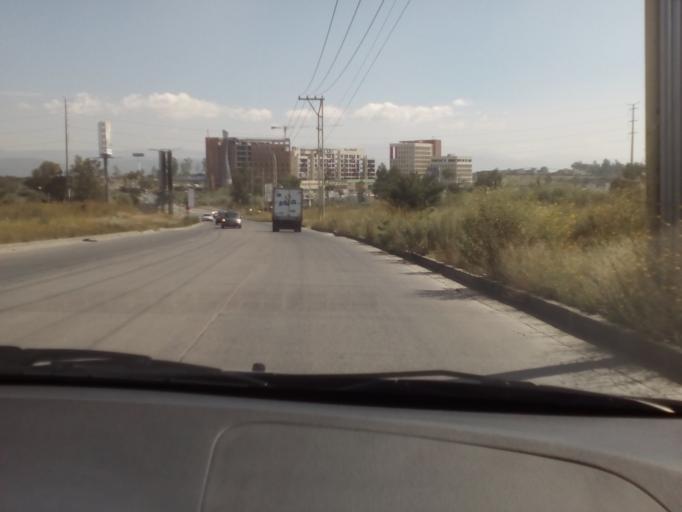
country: MX
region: Guanajuato
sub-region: Leon
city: Fraccionamiento Paseo de las Torres
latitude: 21.1703
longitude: -101.7395
